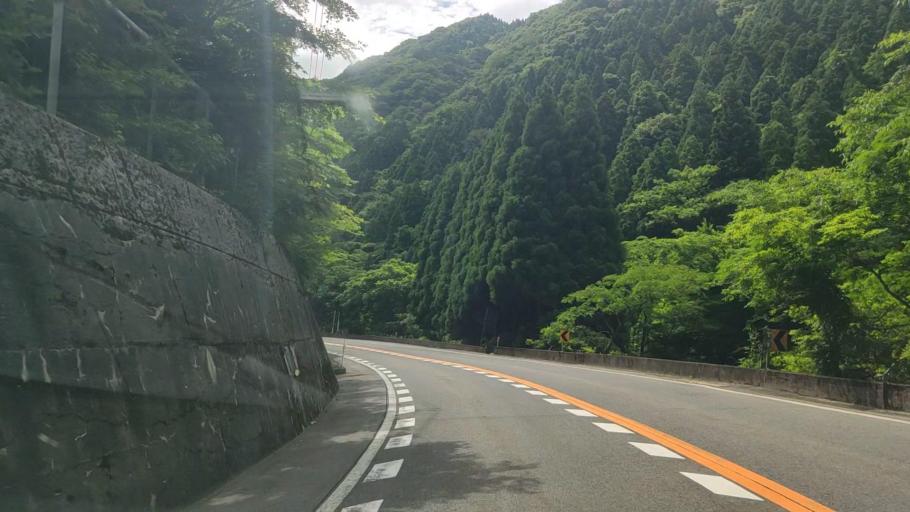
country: JP
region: Okayama
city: Niimi
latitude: 35.2098
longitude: 133.4711
